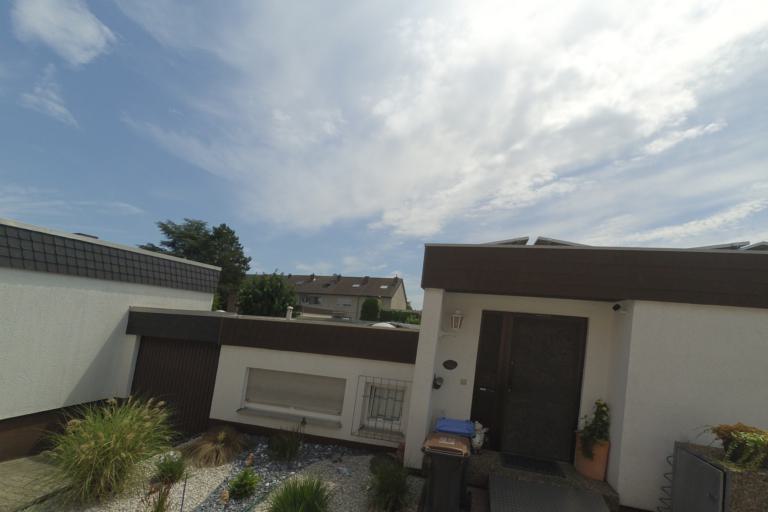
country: DE
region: Rheinland-Pfalz
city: Neuhofen
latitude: 49.4245
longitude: 8.4167
